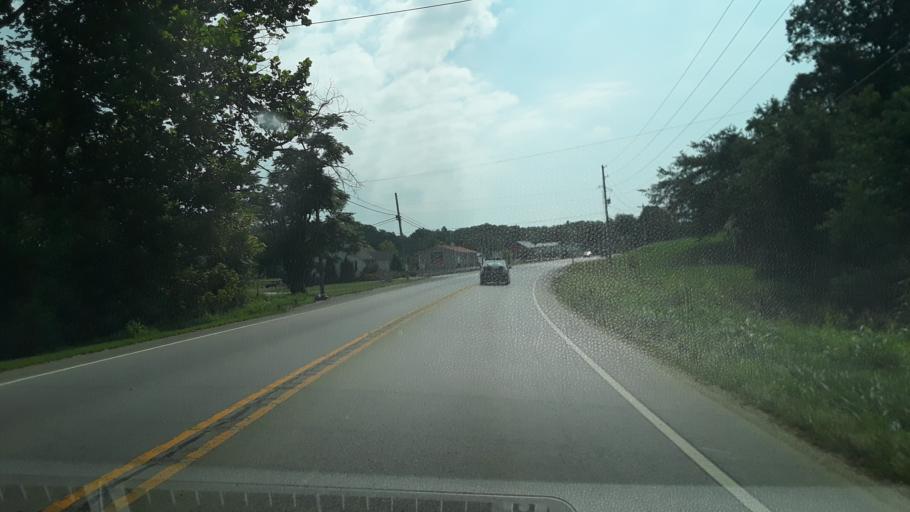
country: US
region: Indiana
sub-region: Clark County
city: Sellersburg
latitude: 38.4446
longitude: -85.8307
